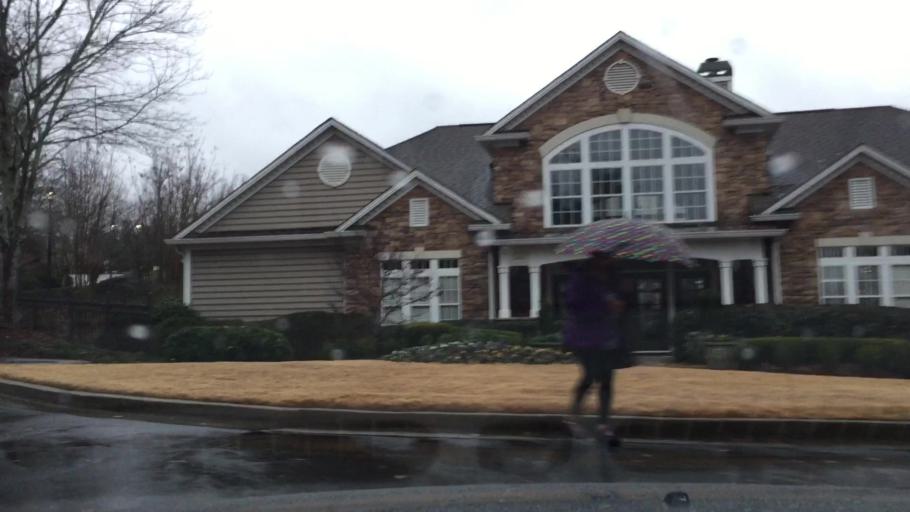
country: US
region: Georgia
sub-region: Cobb County
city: Marietta
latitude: 34.0104
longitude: -84.5546
